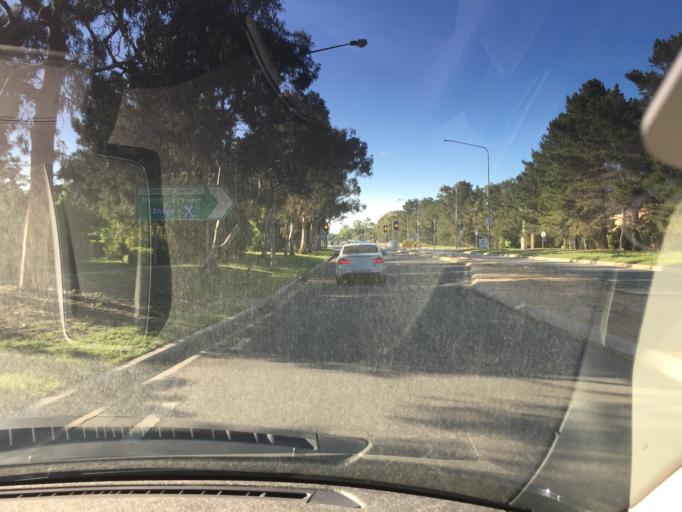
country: AU
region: Australian Capital Territory
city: Kaleen
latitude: -35.2395
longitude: 149.1257
